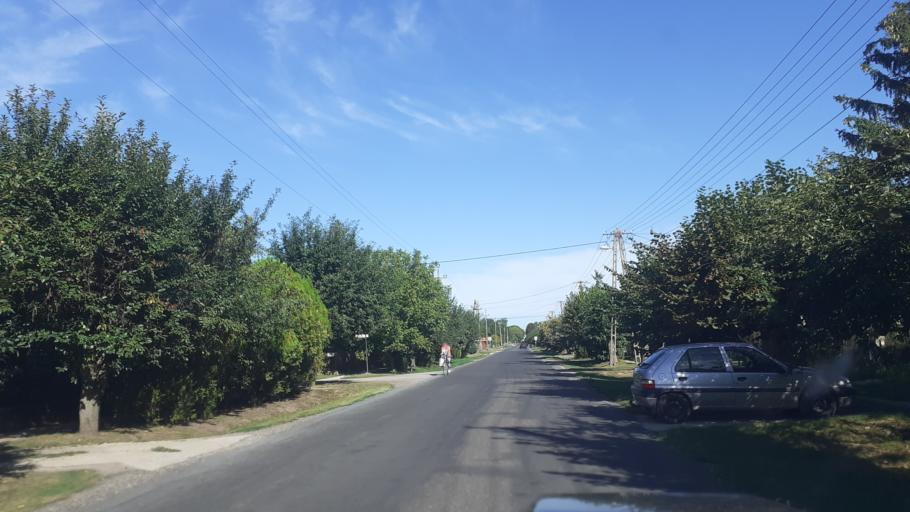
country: HU
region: Fejer
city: Ivancsa
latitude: 47.1856
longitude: 18.8001
